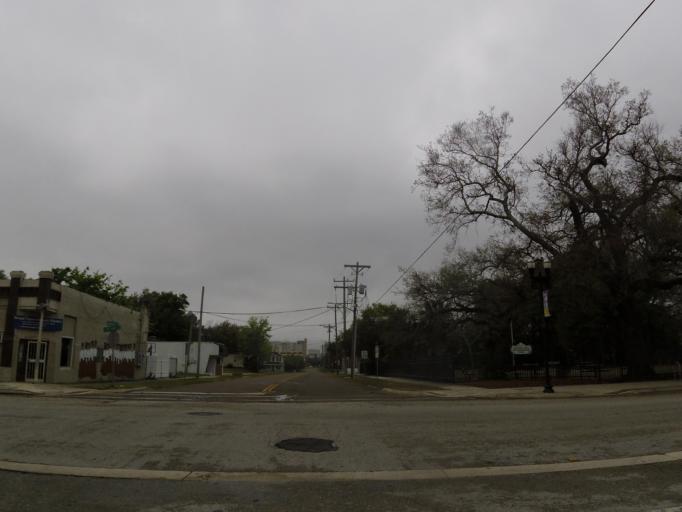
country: US
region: Florida
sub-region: Duval County
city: Jacksonville
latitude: 30.3313
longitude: -81.6424
